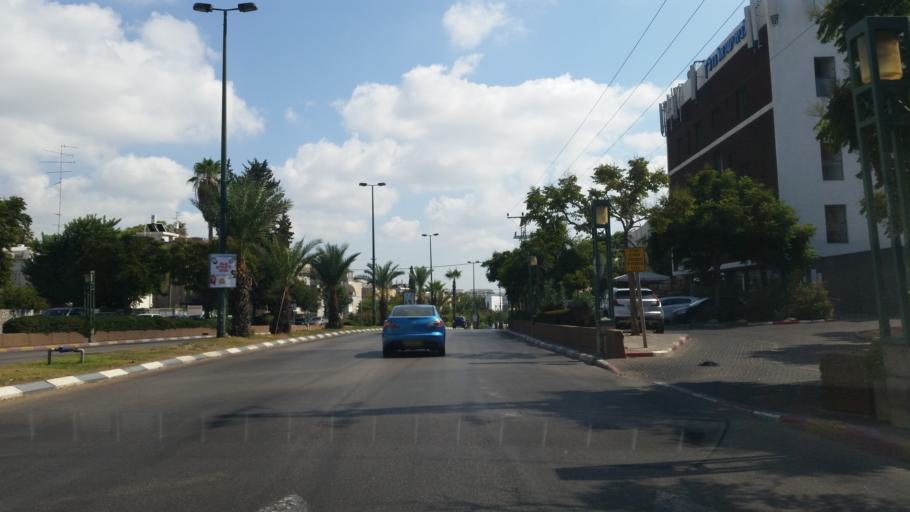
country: IL
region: Tel Aviv
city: Ramat HaSharon
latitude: 32.1212
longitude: 34.8251
